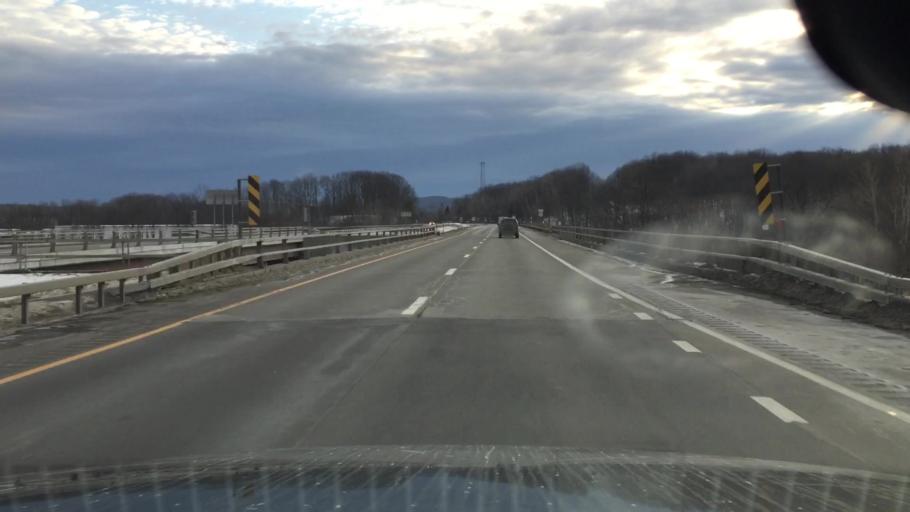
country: US
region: New York
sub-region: Tioga County
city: Waverly
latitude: 42.0000
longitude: -76.5219
